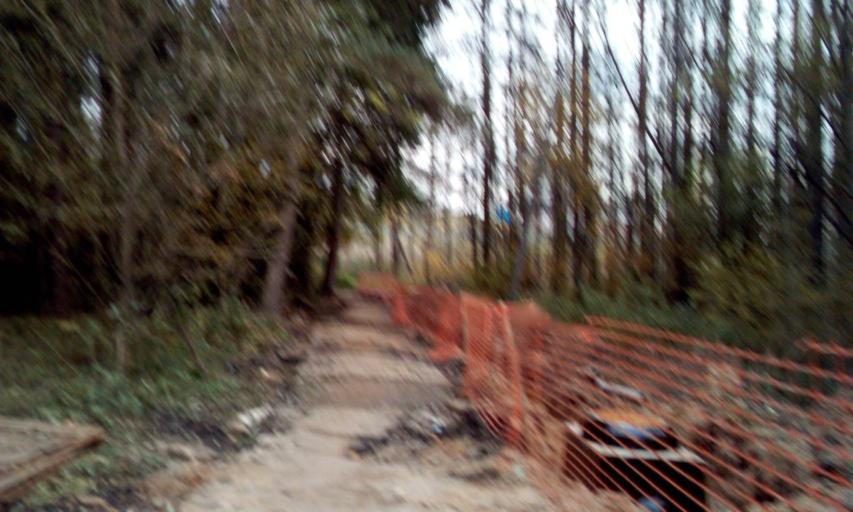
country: RU
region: Moskovskaya
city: Odintsovo
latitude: 55.6844
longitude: 37.2360
